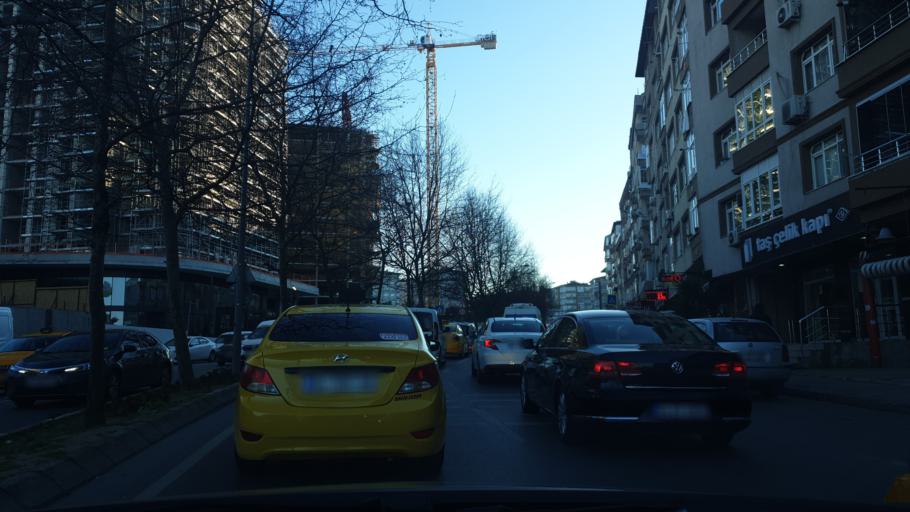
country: TR
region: Istanbul
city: merter keresteciler
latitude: 41.0120
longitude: 28.8776
